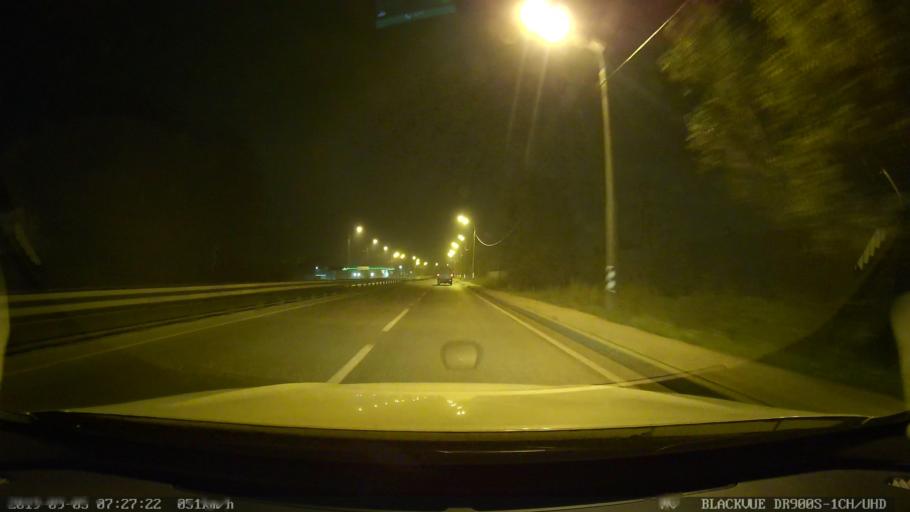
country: RU
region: Moskovskaya
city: Povedniki
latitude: 55.9527
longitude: 37.6497
